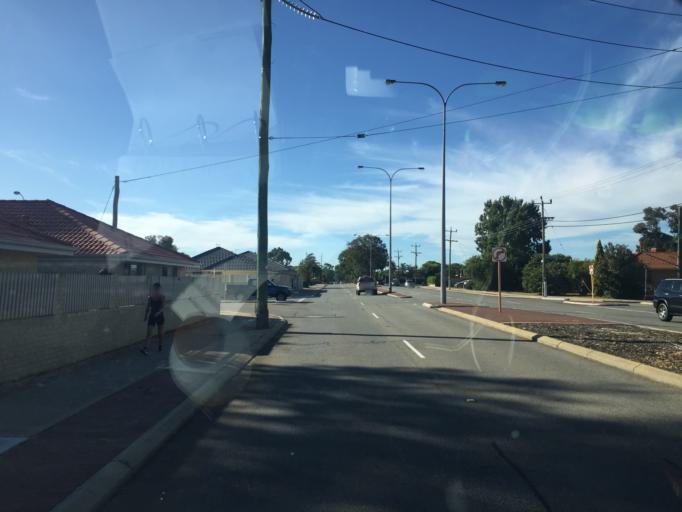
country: AU
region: Western Australia
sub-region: Belmont
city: Kewdale
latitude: -31.9665
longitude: 115.9409
